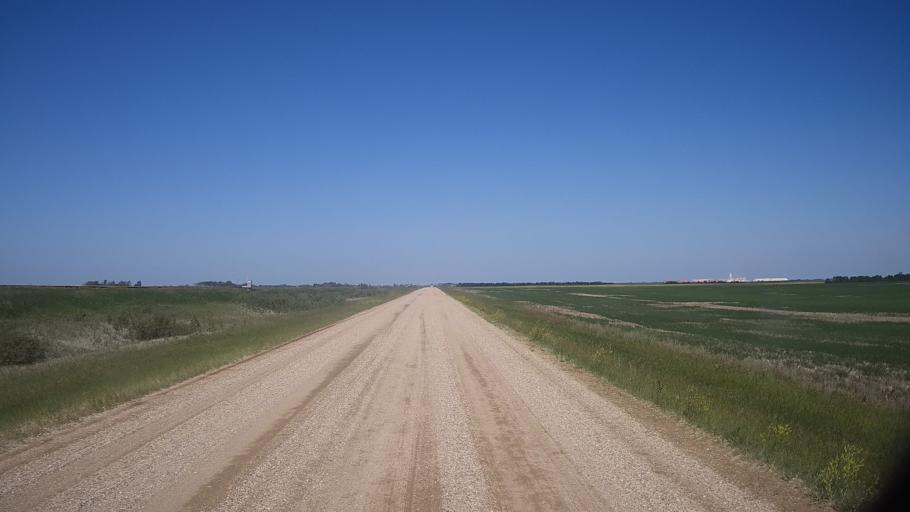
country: CA
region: Saskatchewan
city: Watrous
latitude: 51.8691
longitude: -105.9880
